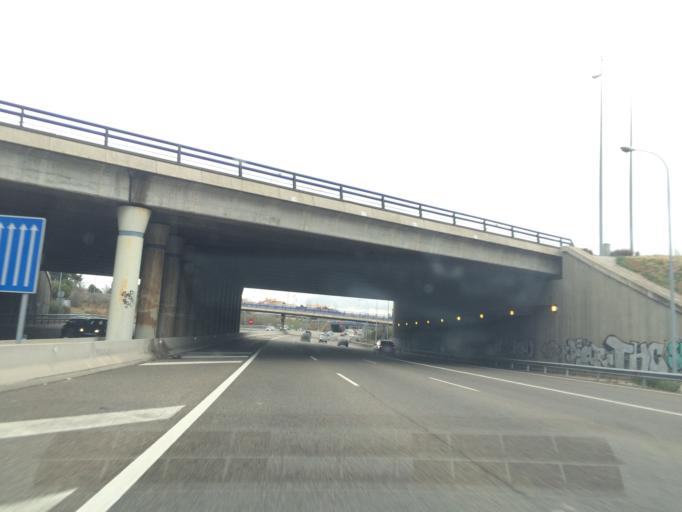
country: ES
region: Madrid
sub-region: Provincia de Madrid
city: Pozuelo de Alarcon
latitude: 40.4644
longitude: -3.7960
